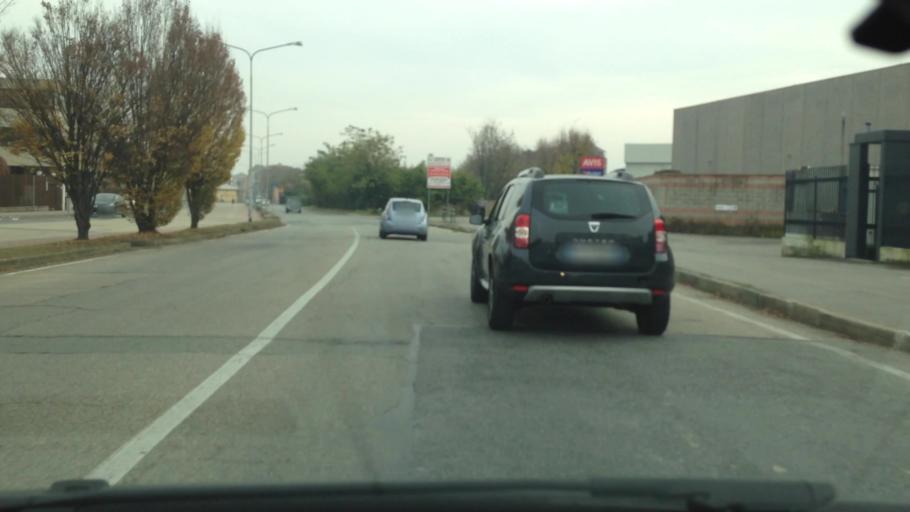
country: IT
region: Piedmont
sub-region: Provincia di Torino
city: Venaria Reale
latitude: 45.1121
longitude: 7.6497
